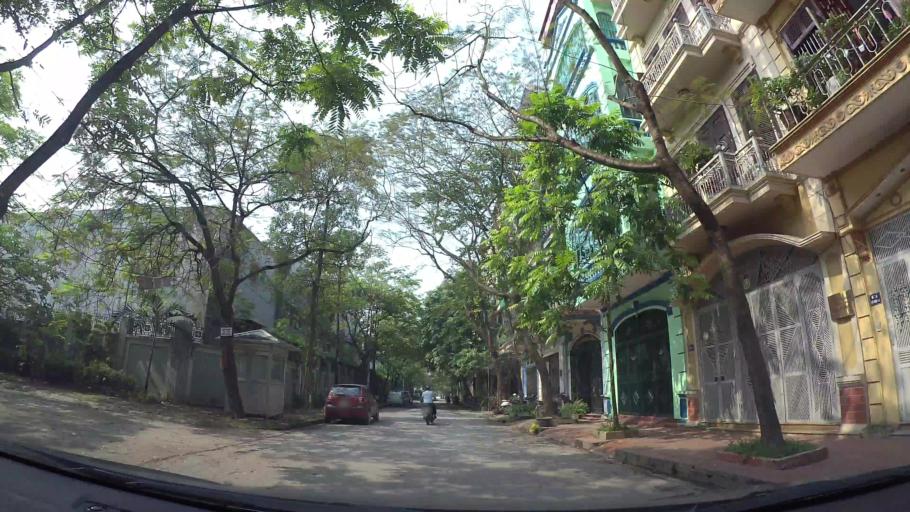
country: VN
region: Ha Noi
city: Van Dien
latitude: 20.9741
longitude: 105.8344
